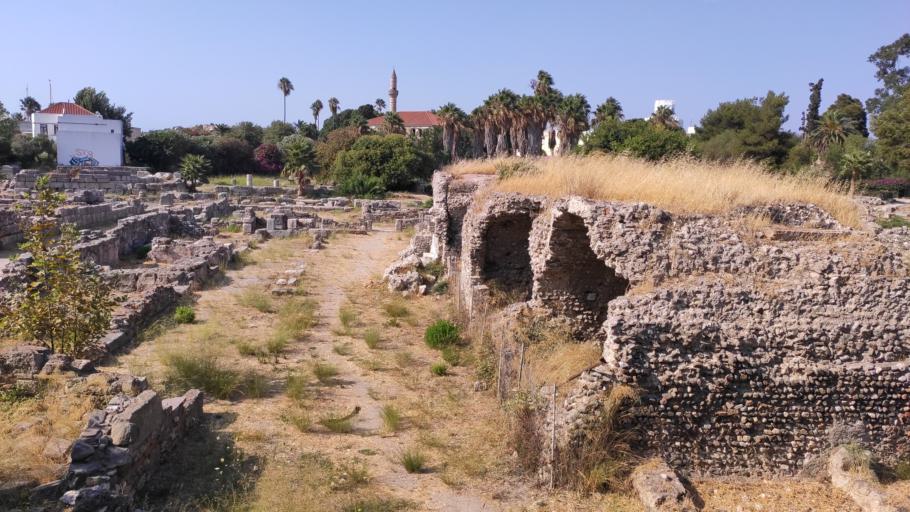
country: GR
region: South Aegean
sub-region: Nomos Dodekanisou
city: Kos
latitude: 36.8930
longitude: 27.2908
